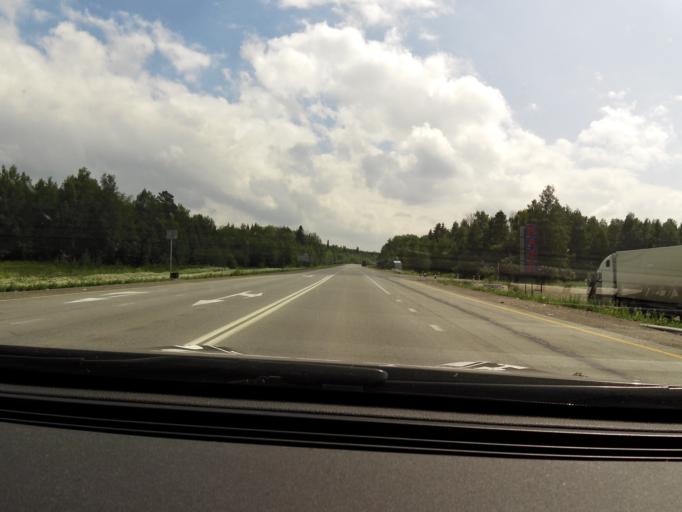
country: RU
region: Perm
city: Suksun
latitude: 57.0152
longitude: 57.4684
